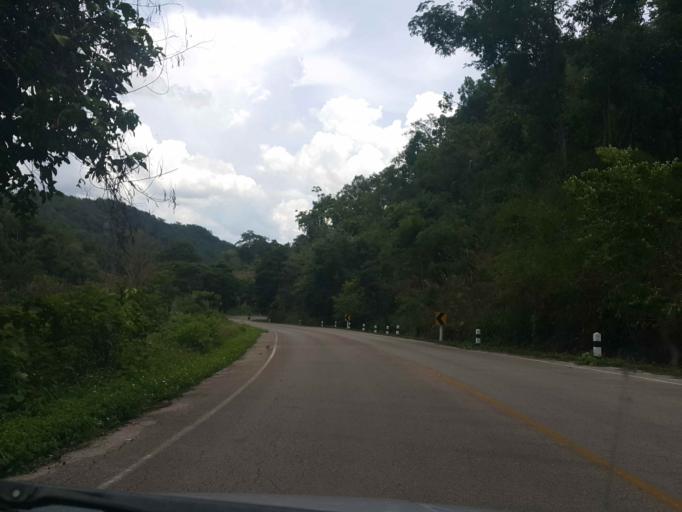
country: TH
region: Phayao
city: Chiang Muan
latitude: 18.9158
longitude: 100.1141
